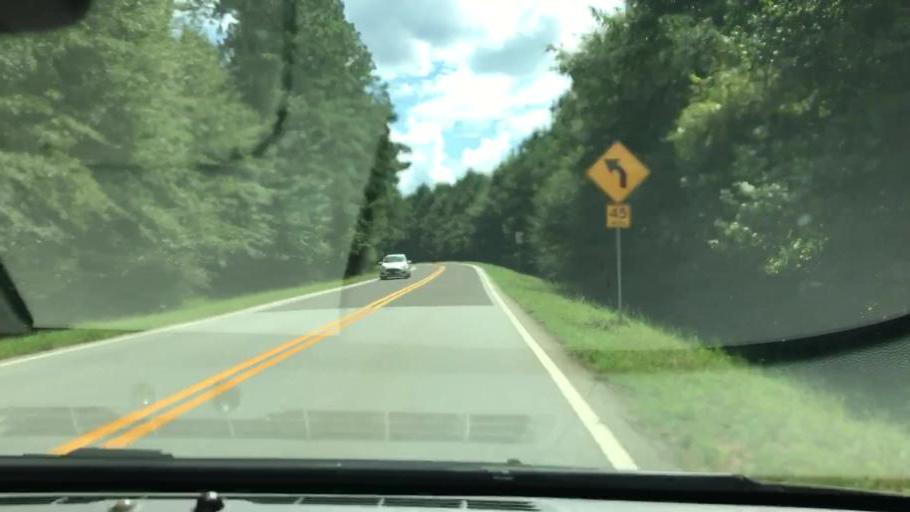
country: US
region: Georgia
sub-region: Quitman County
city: Georgetown
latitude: 31.9833
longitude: -85.0503
